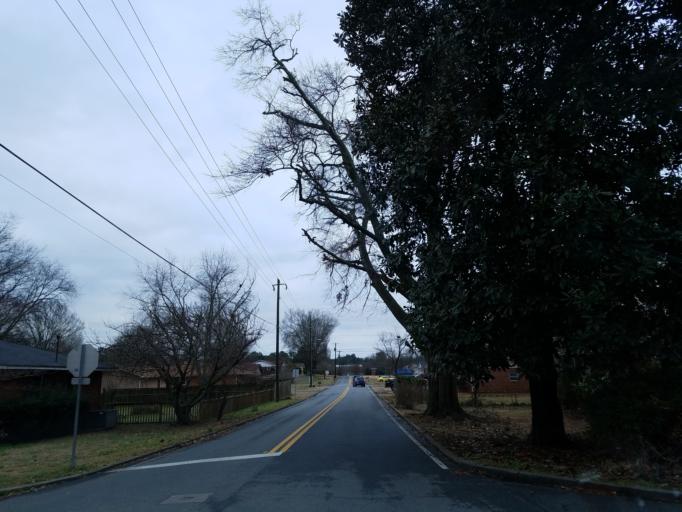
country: US
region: Georgia
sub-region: Bartow County
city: Cartersville
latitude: 34.1553
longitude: -84.7989
